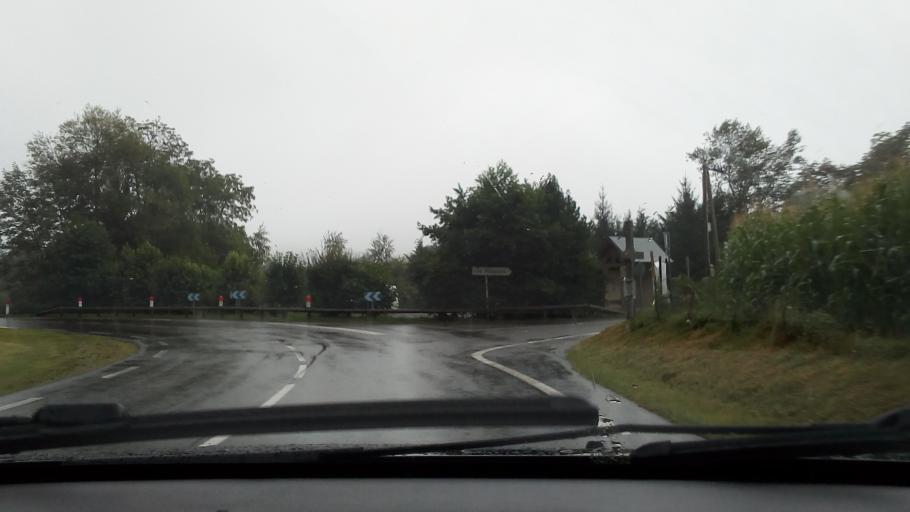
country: FR
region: Midi-Pyrenees
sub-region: Departement des Hautes-Pyrenees
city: Argeles-Gazost
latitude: 42.9747
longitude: -0.1881
